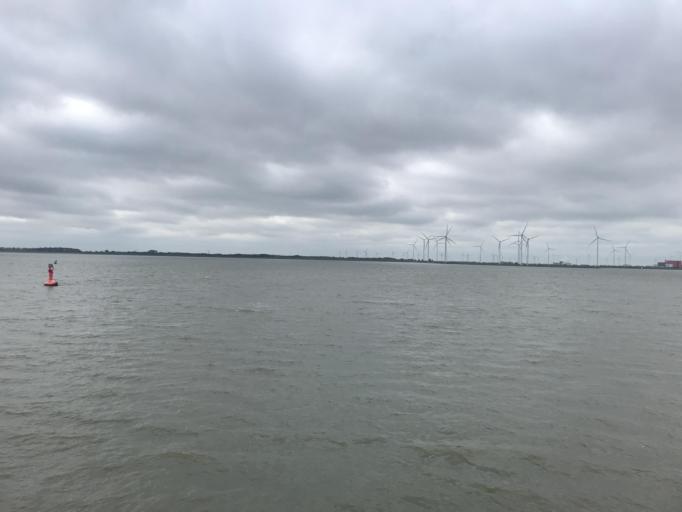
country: NL
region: Groningen
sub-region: Gemeente Delfzijl
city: Delfzijl
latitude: 53.3261
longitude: 7.0313
